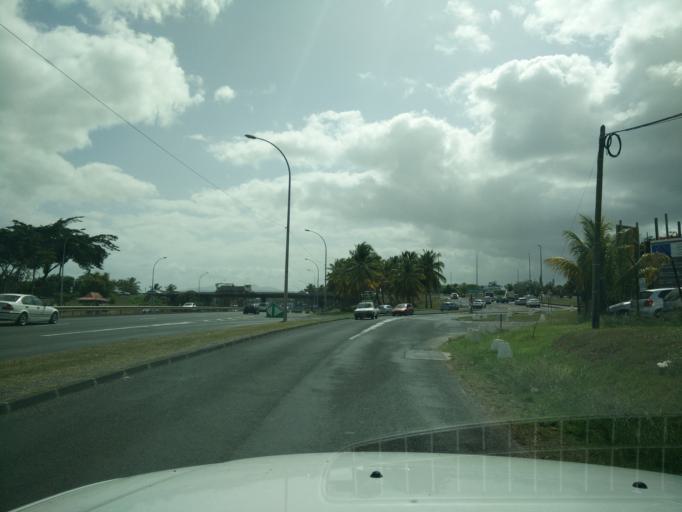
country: GP
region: Guadeloupe
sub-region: Guadeloupe
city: Baie-Mahault
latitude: 16.2544
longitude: -61.5690
